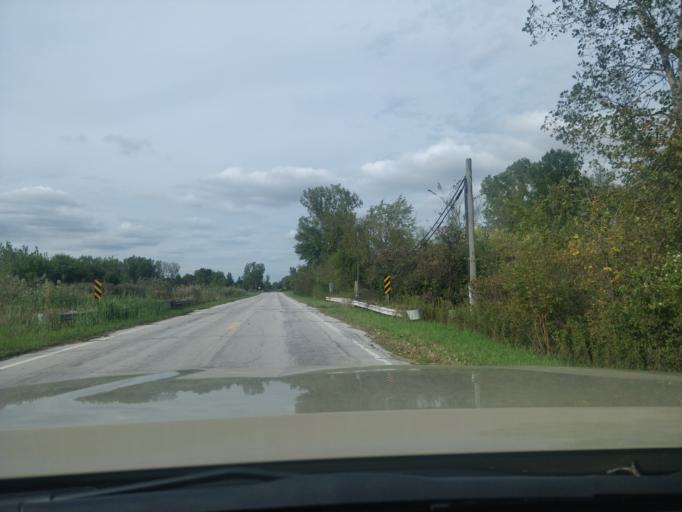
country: US
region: Michigan
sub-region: Wayne County
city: Romulus
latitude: 42.1685
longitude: -83.3642
